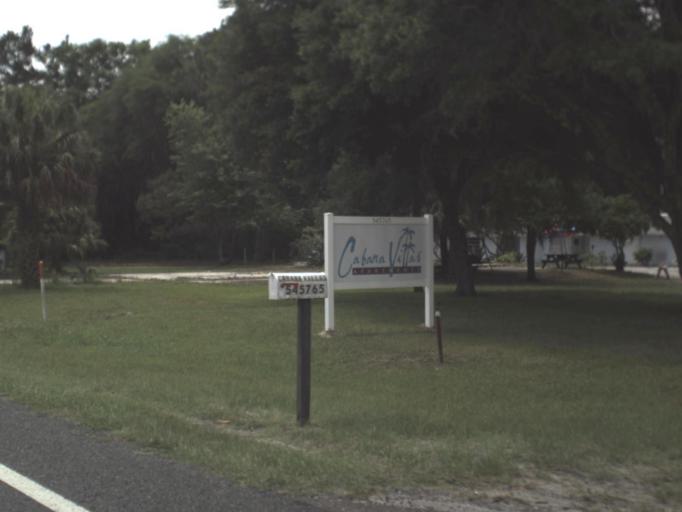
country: US
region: Florida
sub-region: Nassau County
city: Hilliard
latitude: 30.6489
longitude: -81.8729
